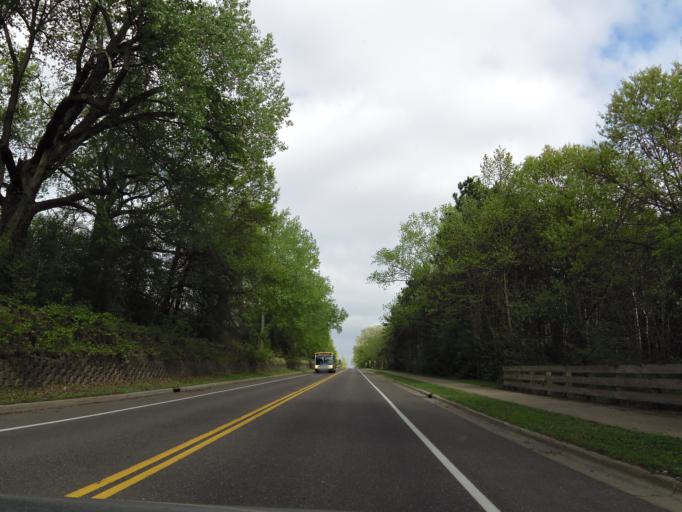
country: US
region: Minnesota
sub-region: Ramsey County
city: Maplewood
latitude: 44.9411
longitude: -92.9972
